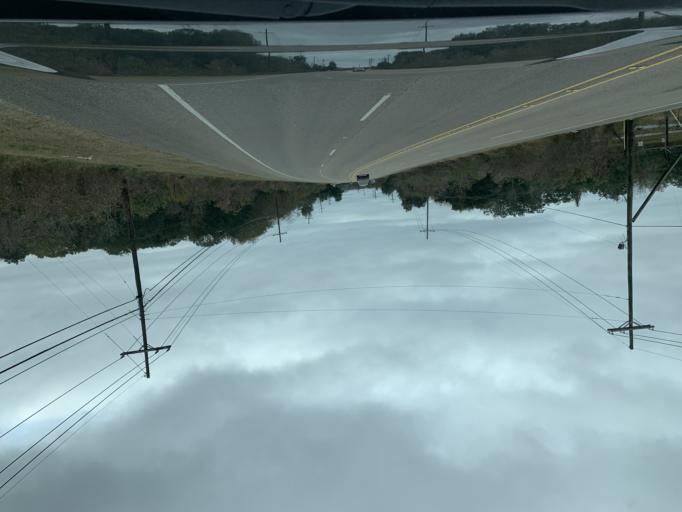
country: US
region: Louisiana
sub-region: Jefferson Parish
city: Bridge City
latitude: 29.9189
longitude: -90.1831
